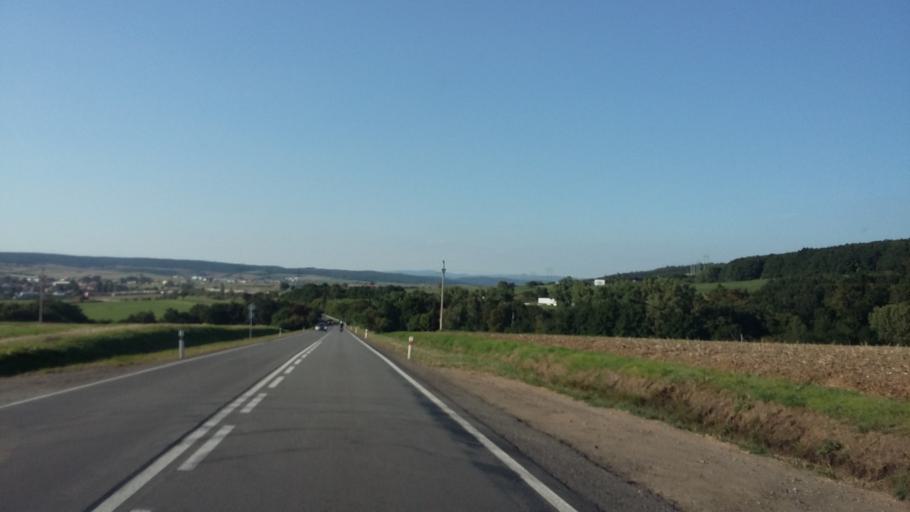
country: CZ
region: South Moravian
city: Ricany
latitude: 49.1939
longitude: 16.4250
